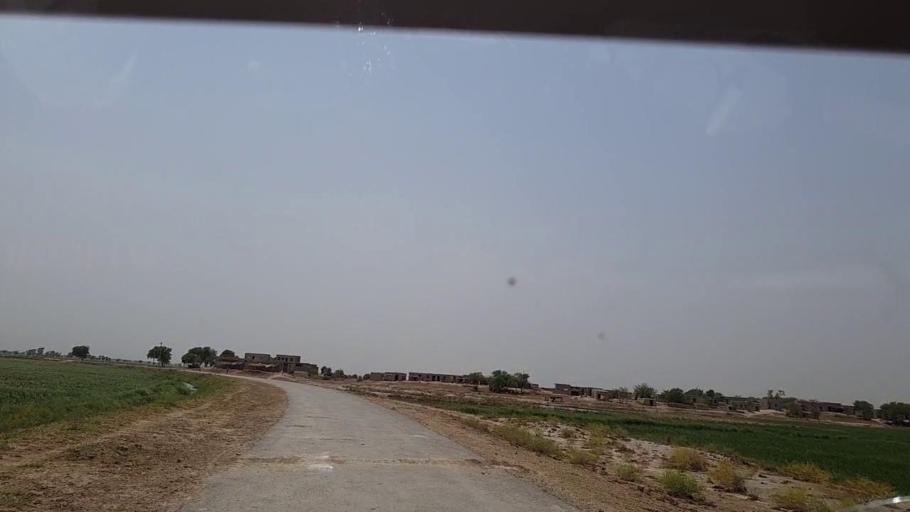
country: PK
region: Sindh
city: Khairpur Nathan Shah
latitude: 27.0180
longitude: 67.6600
